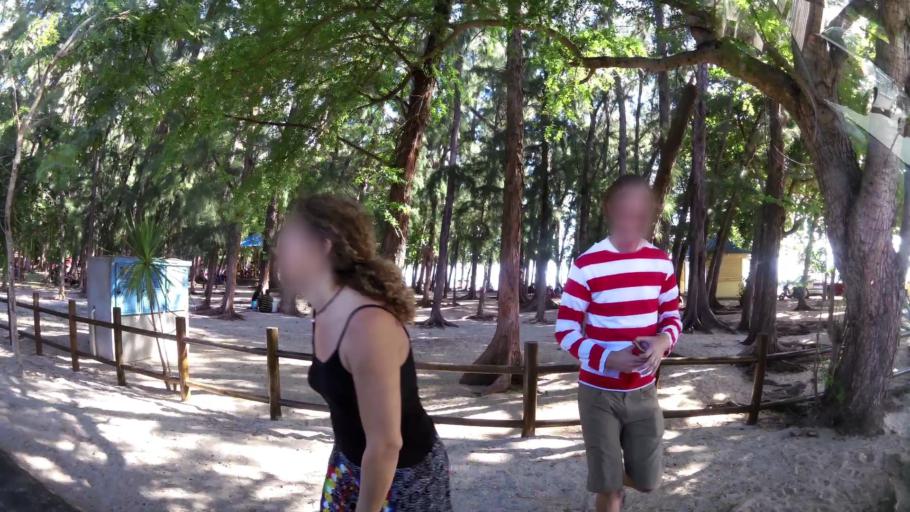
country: MU
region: Black River
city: Albion
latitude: -20.2089
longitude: 57.4045
